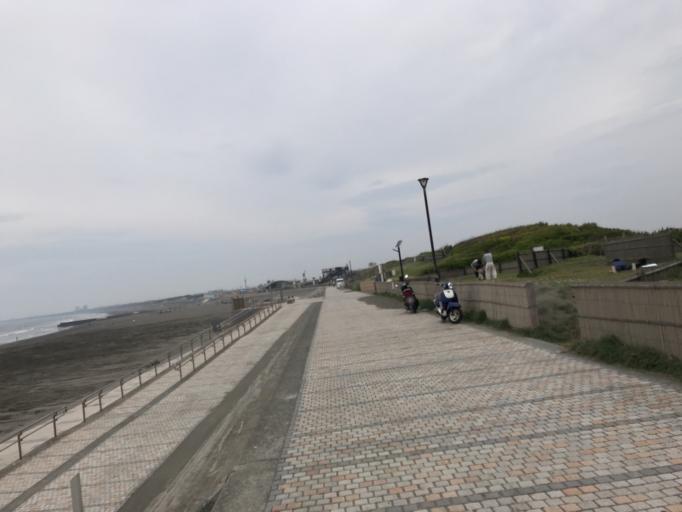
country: JP
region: Kanagawa
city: Fujisawa
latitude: 35.3140
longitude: 139.4735
